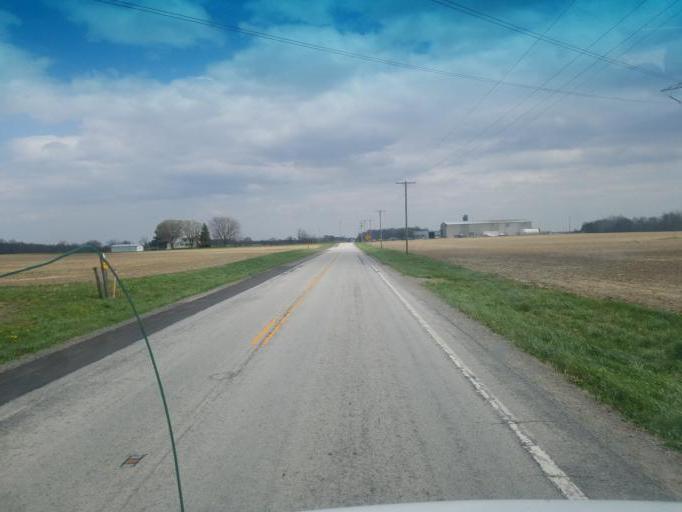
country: US
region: Ohio
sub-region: Wyandot County
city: Upper Sandusky
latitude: 40.9494
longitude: -83.2136
